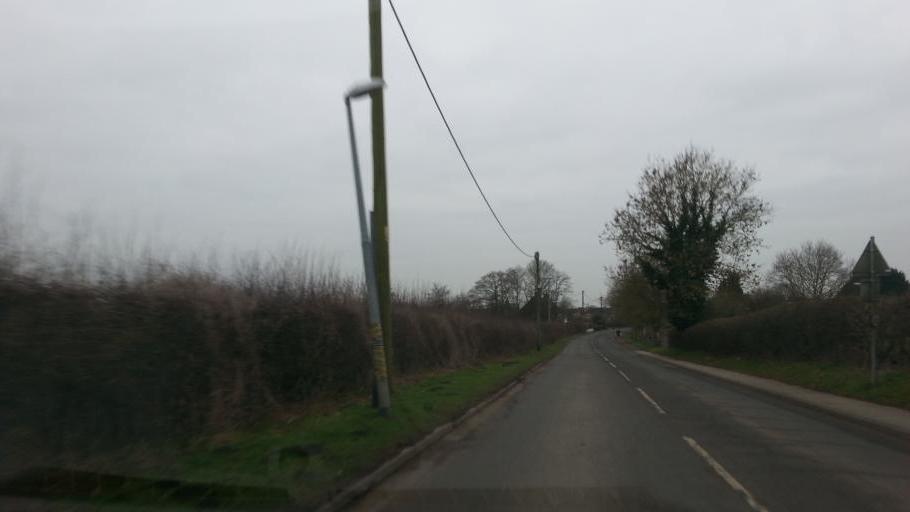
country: GB
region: England
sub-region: Central Bedfordshire
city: Stanbridge
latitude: 51.9080
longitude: -0.5842
